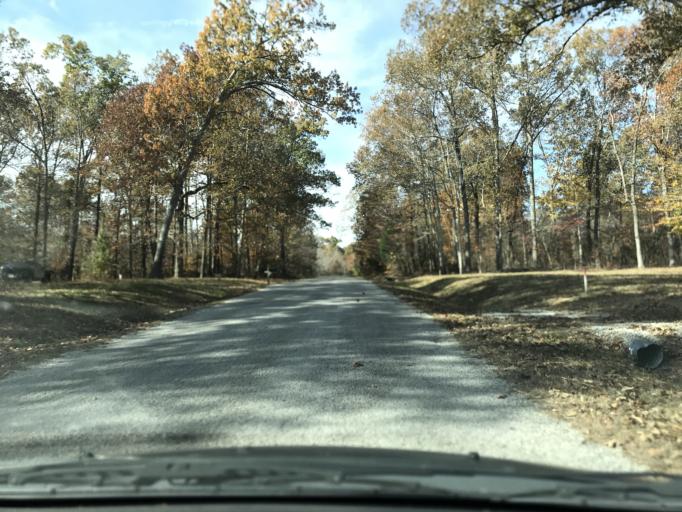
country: US
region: Tennessee
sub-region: Coffee County
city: Tullahoma
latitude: 35.4060
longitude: -86.1709
